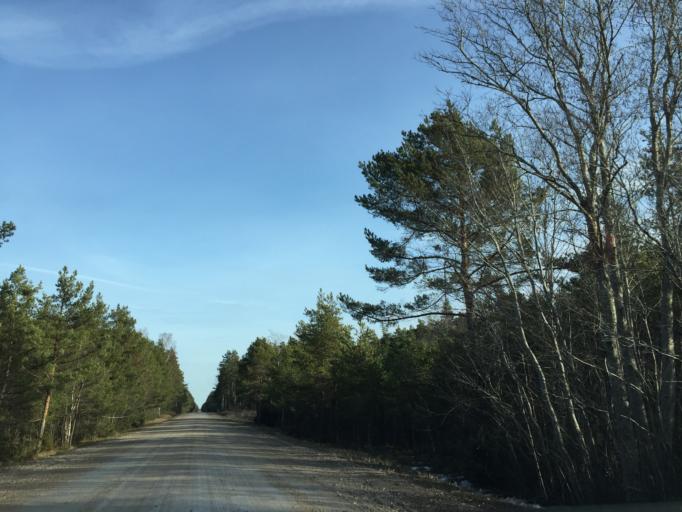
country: EE
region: Saare
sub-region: Kuressaare linn
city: Kuressaare
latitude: 58.3041
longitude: 21.9646
